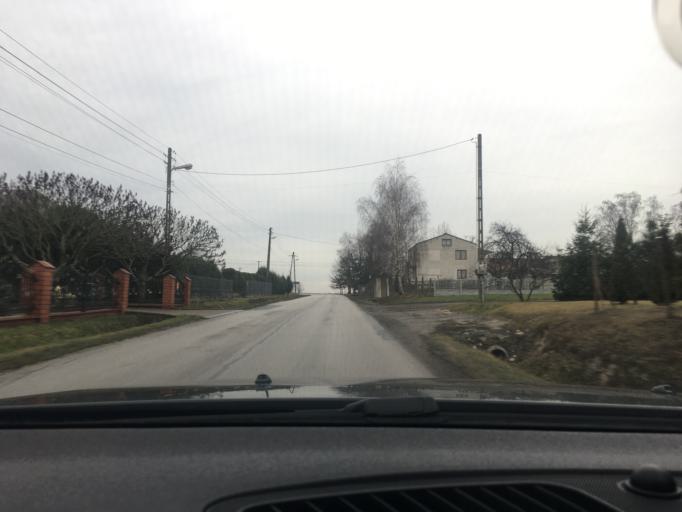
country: PL
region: Swietokrzyskie
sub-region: Powiat jedrzejowski
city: Jedrzejow
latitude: 50.6410
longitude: 20.3494
